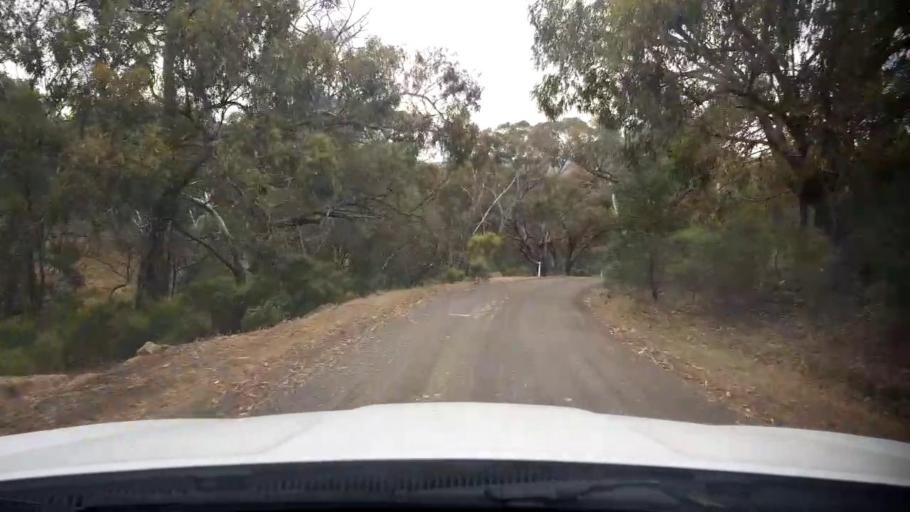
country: AU
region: Victoria
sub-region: Whittlesea
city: Whittlesea
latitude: -37.4877
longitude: 145.0503
